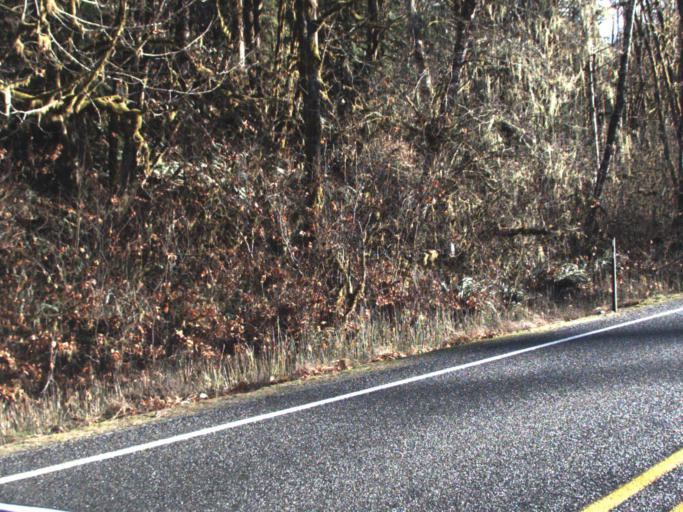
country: US
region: Washington
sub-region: Snohomish County
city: Darrington
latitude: 48.3760
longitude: -121.5476
